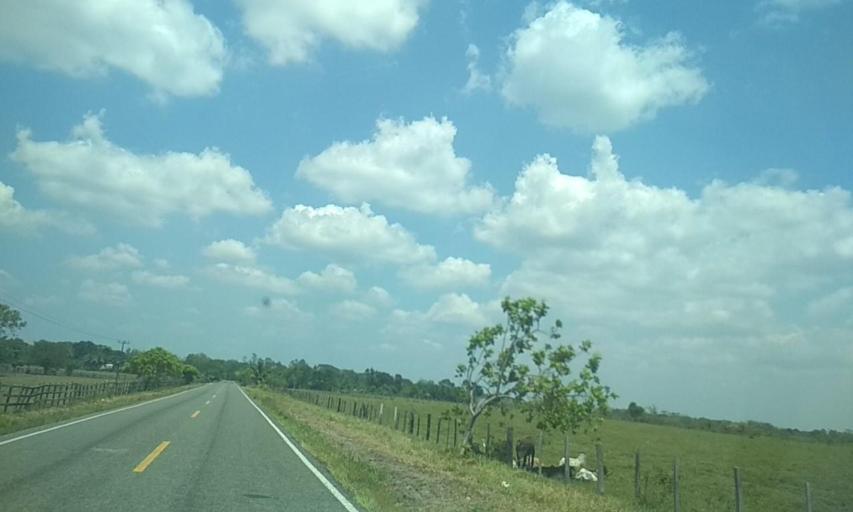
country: MX
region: Tabasco
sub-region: Huimanguillo
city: Huapacal 1ra. Seccion
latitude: 17.7530
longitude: -93.7344
